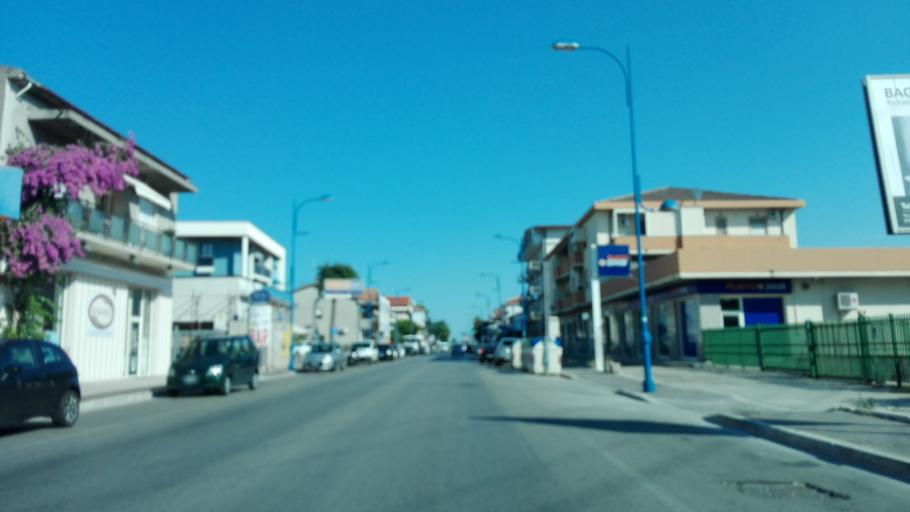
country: IT
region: Abruzzo
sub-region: Provincia di Pescara
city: Montesilvano Marina
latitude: 42.5078
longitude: 14.1605
